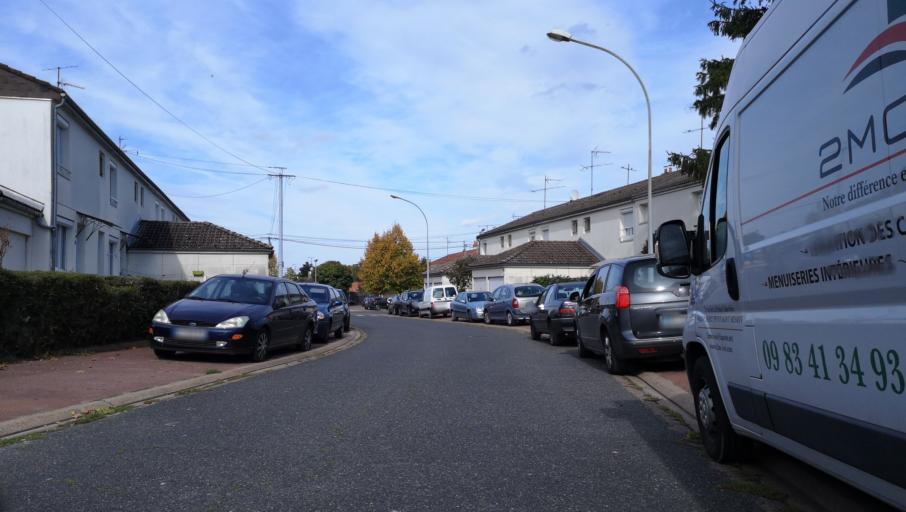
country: FR
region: Centre
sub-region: Departement du Loiret
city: Saint-Jean-de-la-Ruelle
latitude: 47.9246
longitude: 1.8810
